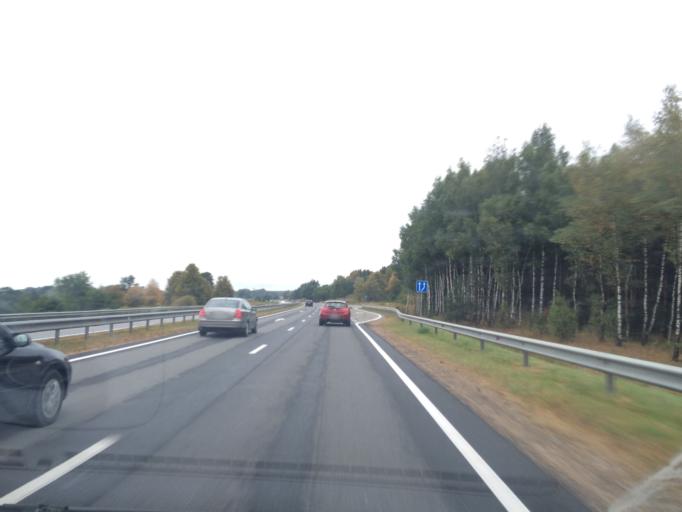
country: LV
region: Ikskile
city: Ikskile
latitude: 56.8441
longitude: 24.4767
